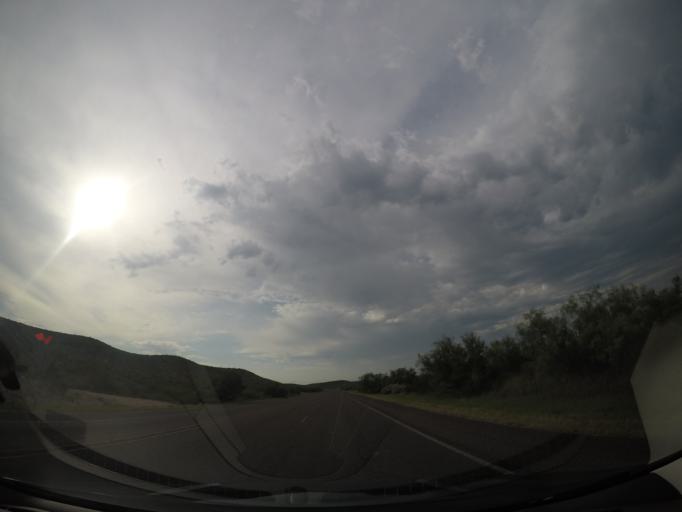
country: US
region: Texas
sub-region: Terrell County
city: Sanderson
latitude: 29.8995
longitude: -101.7990
